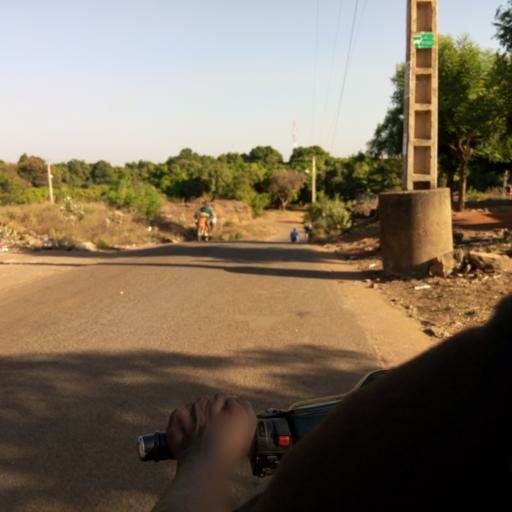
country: ML
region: Bamako
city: Bamako
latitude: 12.6604
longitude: -8.0364
